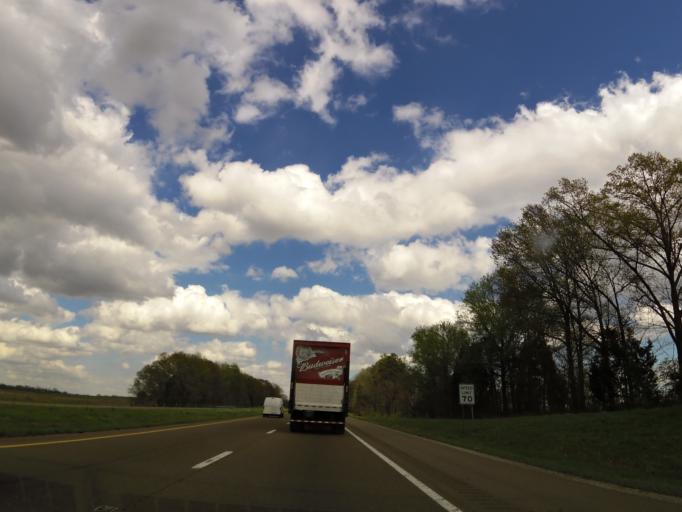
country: US
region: Tennessee
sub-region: Crockett County
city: Bells
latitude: 35.5995
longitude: -89.0480
